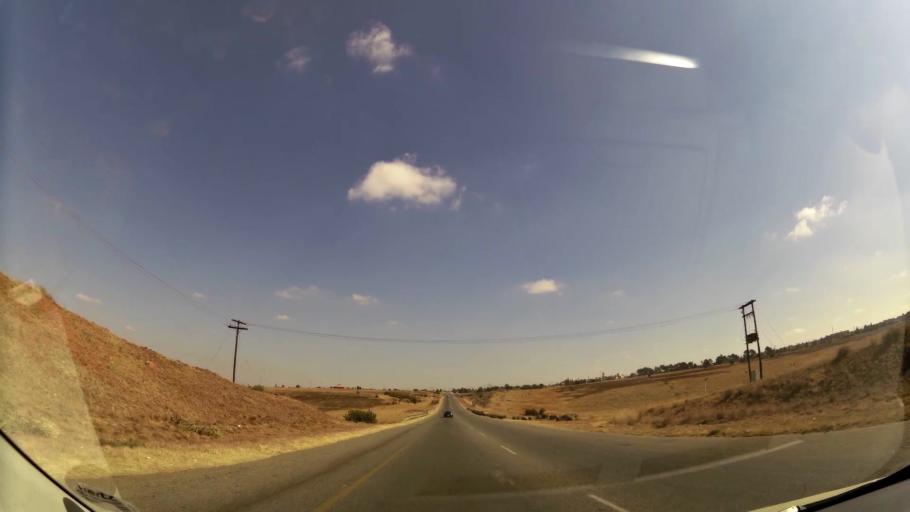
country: ZA
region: Gauteng
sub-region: West Rand District Municipality
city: Randfontein
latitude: -26.1775
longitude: 27.7672
